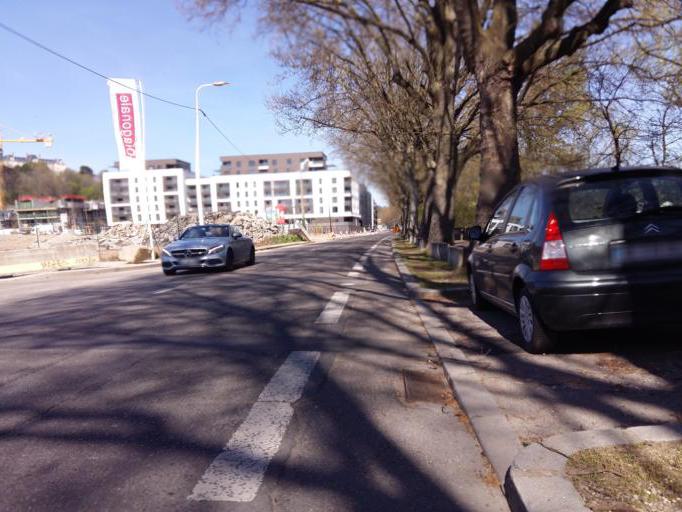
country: FR
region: Rhone-Alpes
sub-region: Departement du Rhone
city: Caluire-et-Cuire
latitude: 45.7888
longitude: 4.8161
